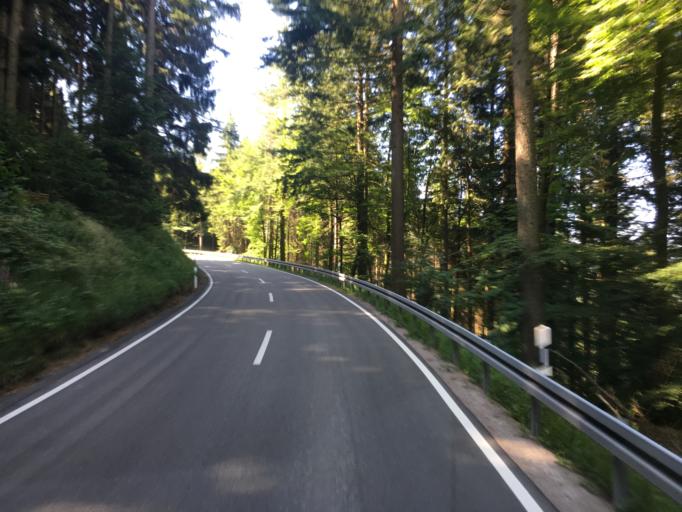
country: DE
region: Baden-Wuerttemberg
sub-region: Freiburg Region
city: Seebach
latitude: 48.5759
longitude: 8.2125
